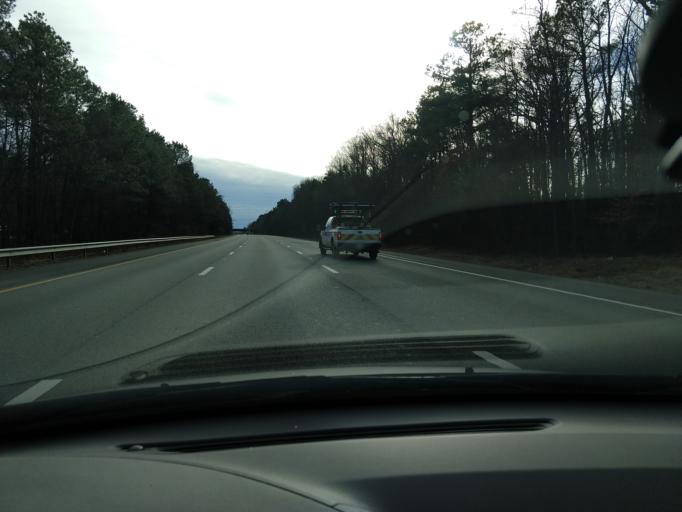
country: US
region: Virginia
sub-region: Hanover County
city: Ashland
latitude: 37.8216
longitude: -77.4574
